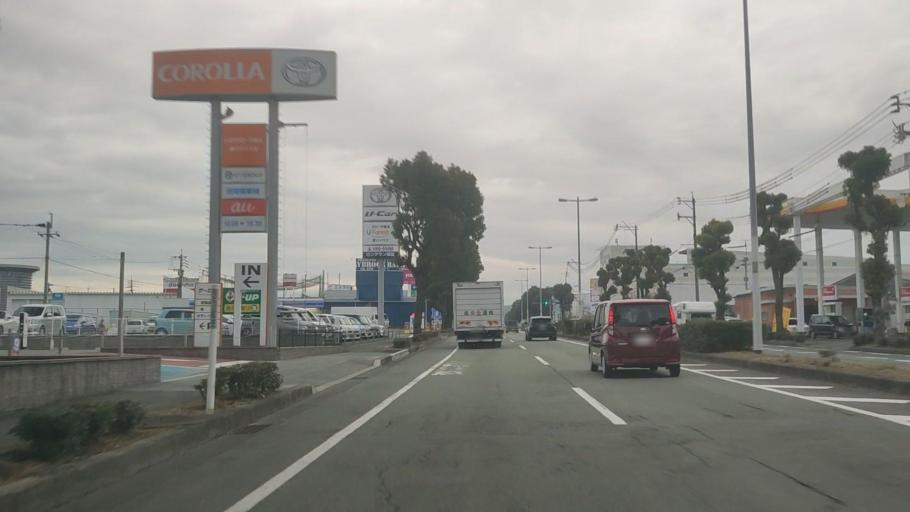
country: JP
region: Kumamoto
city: Kumamoto
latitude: 32.8242
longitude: 130.7628
